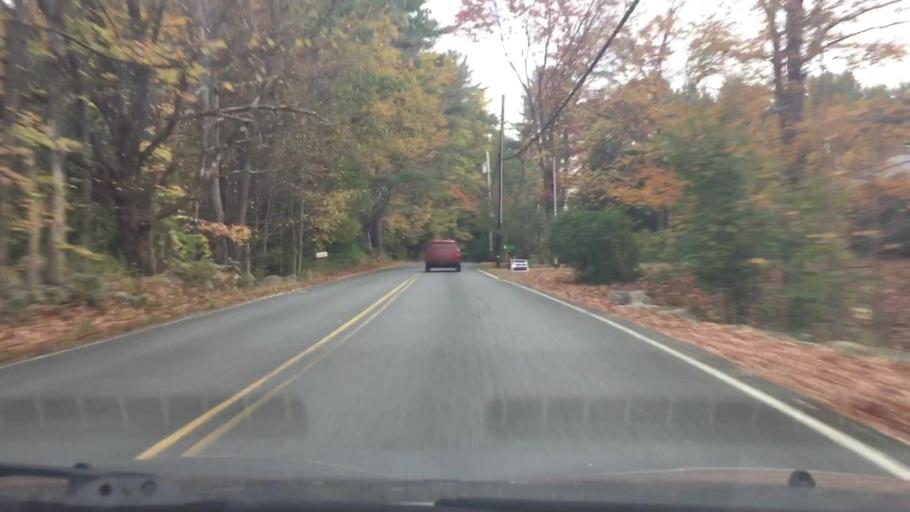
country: US
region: New Hampshire
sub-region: Cheshire County
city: Keene
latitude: 42.9039
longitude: -72.2877
